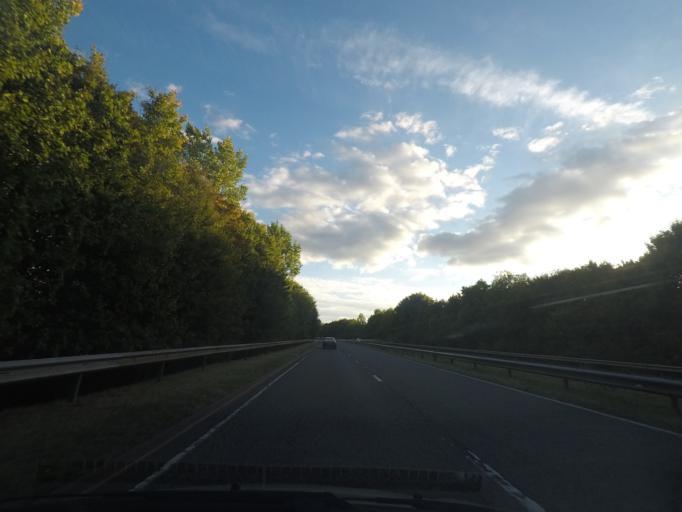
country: GB
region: England
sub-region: Oxfordshire
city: Boars Hill
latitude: 51.7430
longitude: -1.3224
